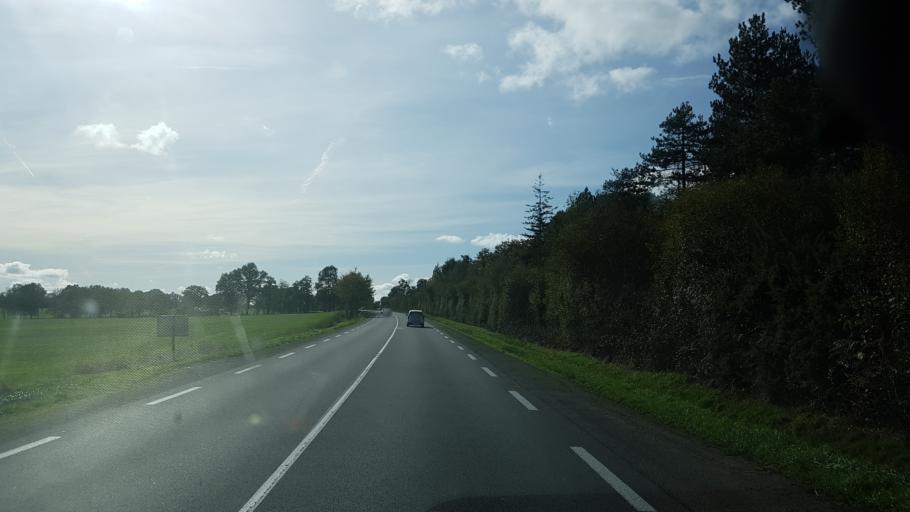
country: FR
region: Poitou-Charentes
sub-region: Departement de la Charente
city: Confolens
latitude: 45.9870
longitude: 0.6082
